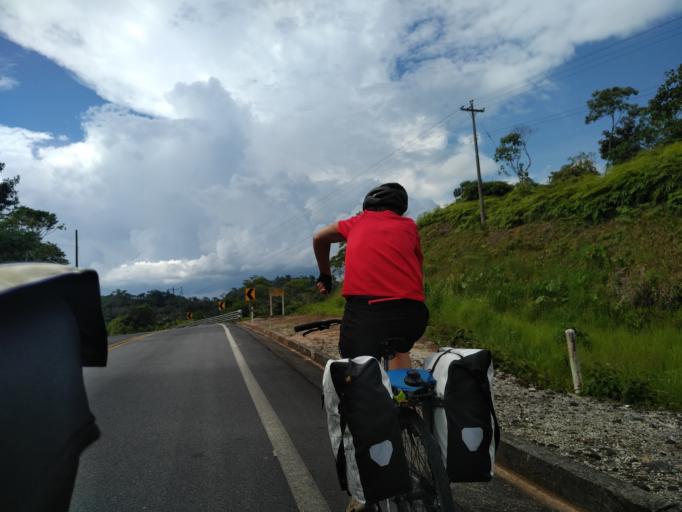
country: EC
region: Napo
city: Tena
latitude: -1.0862
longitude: -77.7900
